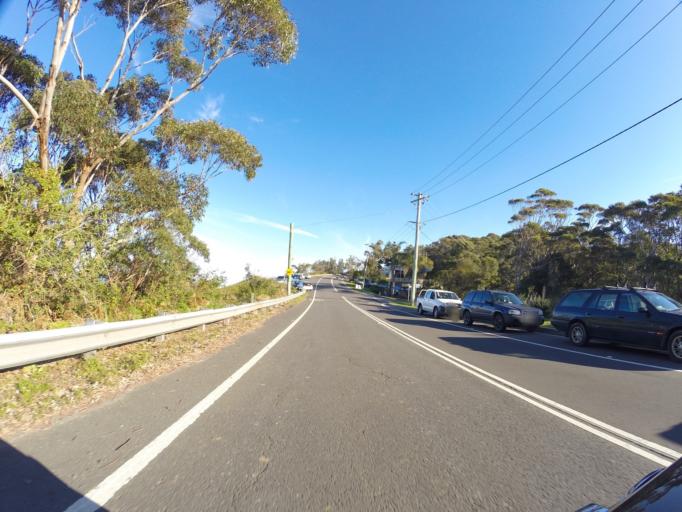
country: AU
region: New South Wales
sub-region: Wollongong
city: Helensburgh
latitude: -34.2141
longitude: 151.0067
